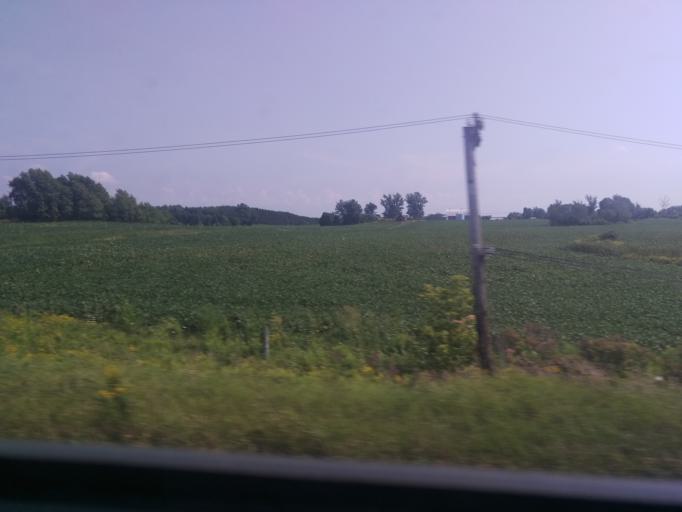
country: US
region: New York
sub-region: Jefferson County
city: Alexandria Bay
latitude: 44.4541
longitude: -75.9274
